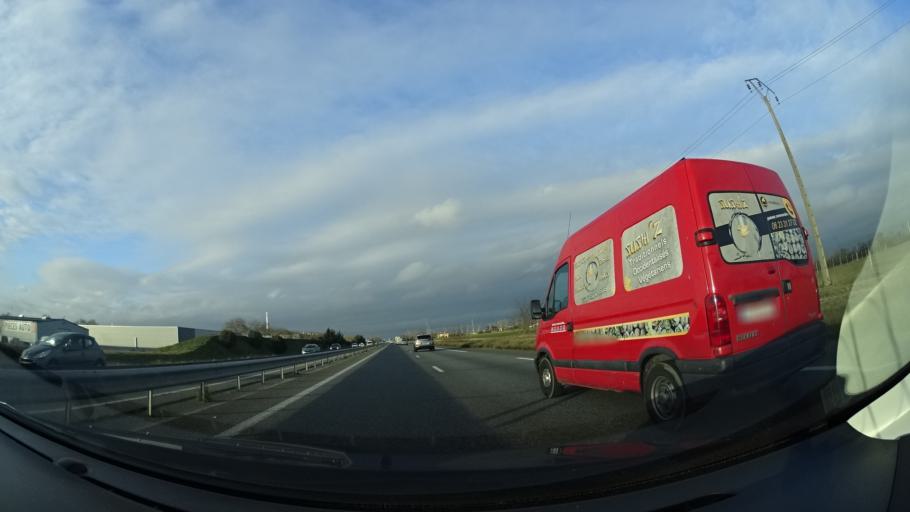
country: FR
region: Midi-Pyrenees
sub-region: Departement de l'Ariege
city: La Tour-du-Crieu
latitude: 43.1099
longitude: 1.6316
